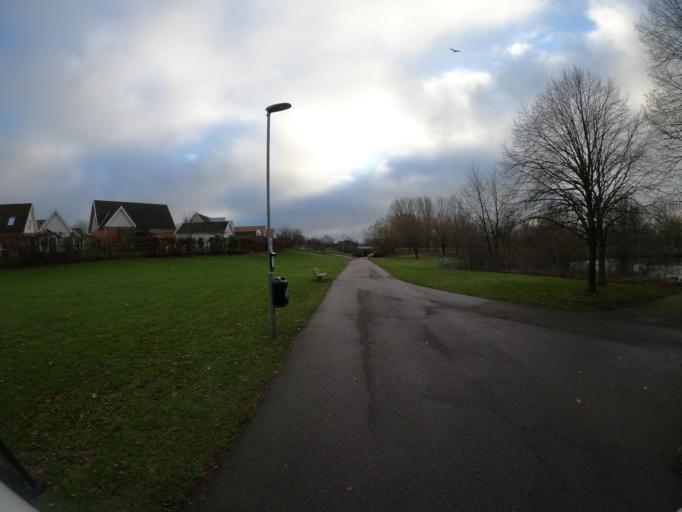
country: SE
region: Skane
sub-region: Svedala Kommun
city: Svedala
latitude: 55.5193
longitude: 13.2171
